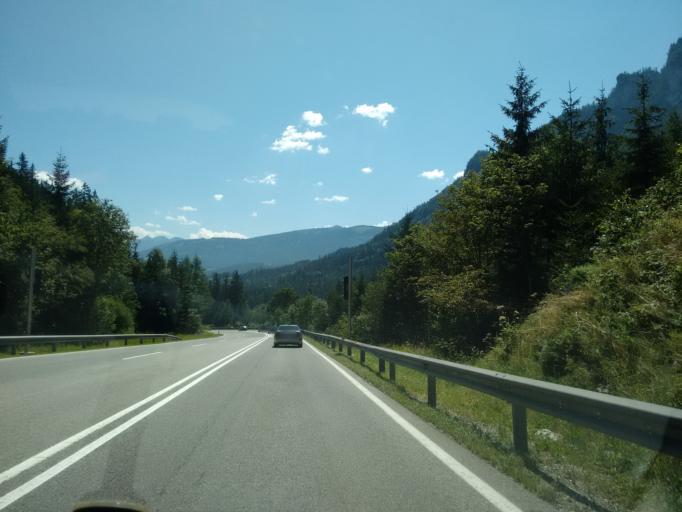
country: AT
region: Styria
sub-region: Politischer Bezirk Liezen
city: Irdning
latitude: 47.5293
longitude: 14.0572
